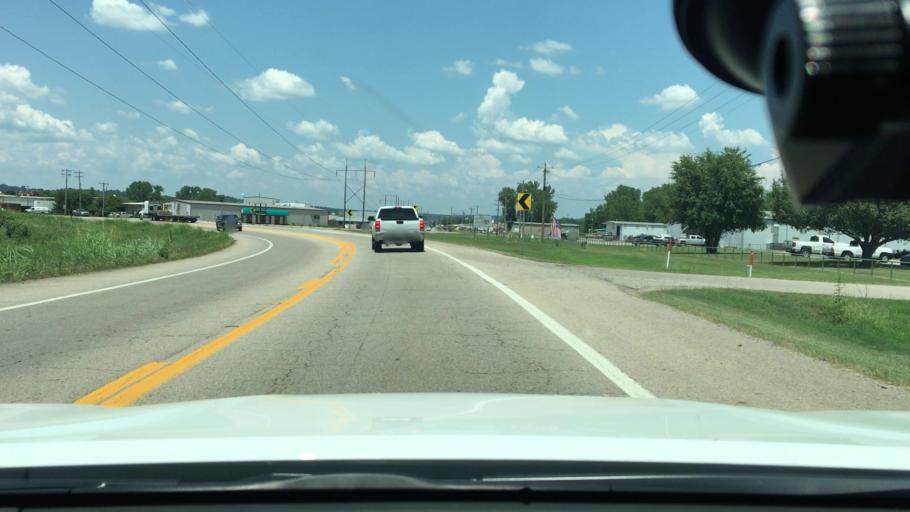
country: US
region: Arkansas
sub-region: Crawford County
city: Van Buren
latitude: 35.4127
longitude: -94.3298
